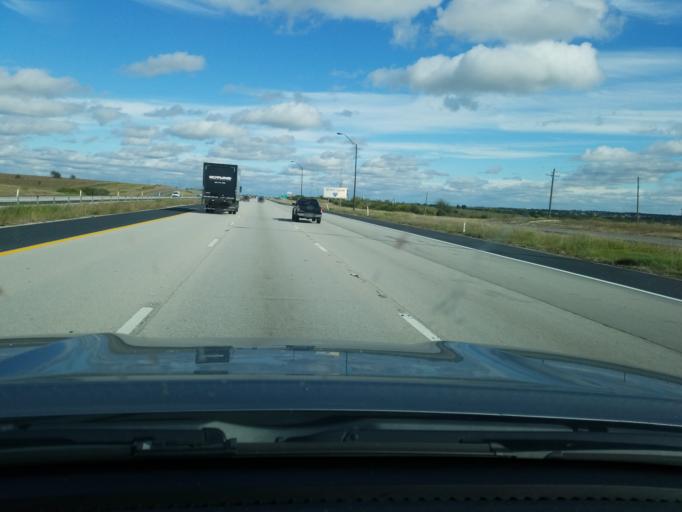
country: US
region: Texas
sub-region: Parker County
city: Aledo
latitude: 32.7209
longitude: -97.5488
